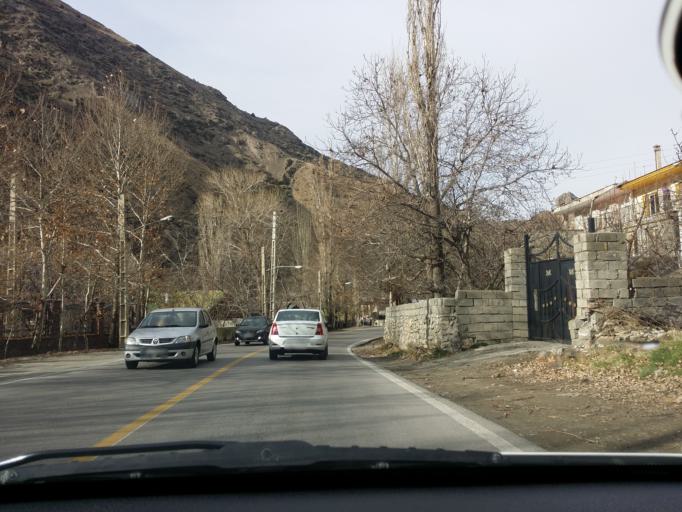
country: IR
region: Tehran
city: Tajrish
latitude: 36.0292
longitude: 51.2372
